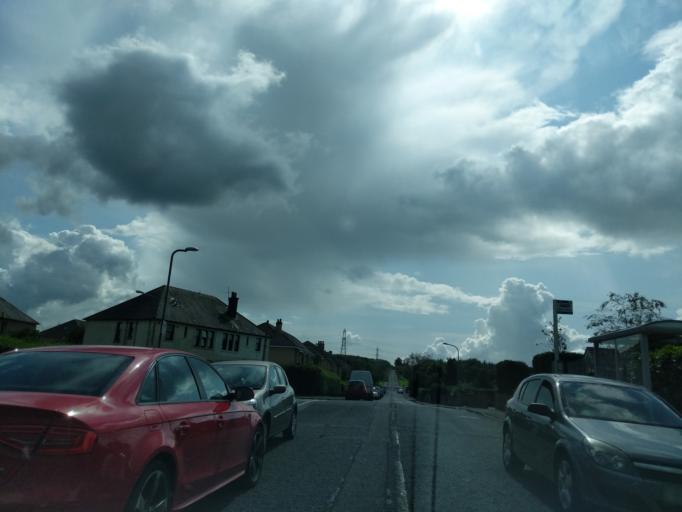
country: GB
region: Scotland
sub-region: East Renfrewshire
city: Neilston
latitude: 55.7799
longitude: -4.4280
